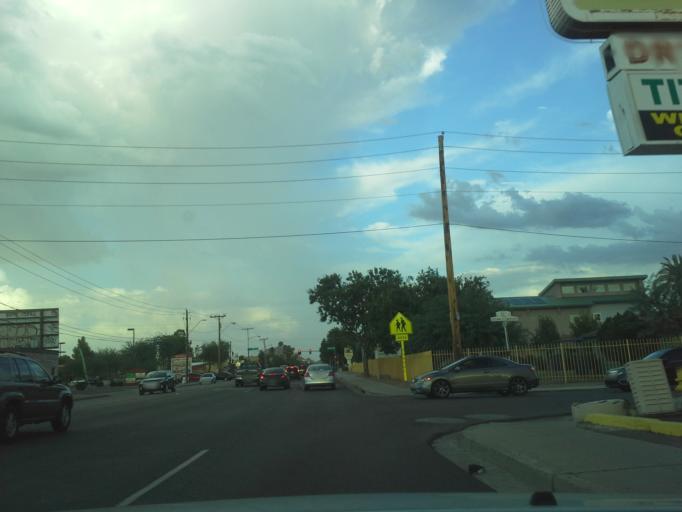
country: US
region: Arizona
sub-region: Maricopa County
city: Phoenix
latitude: 33.4657
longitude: -112.0064
